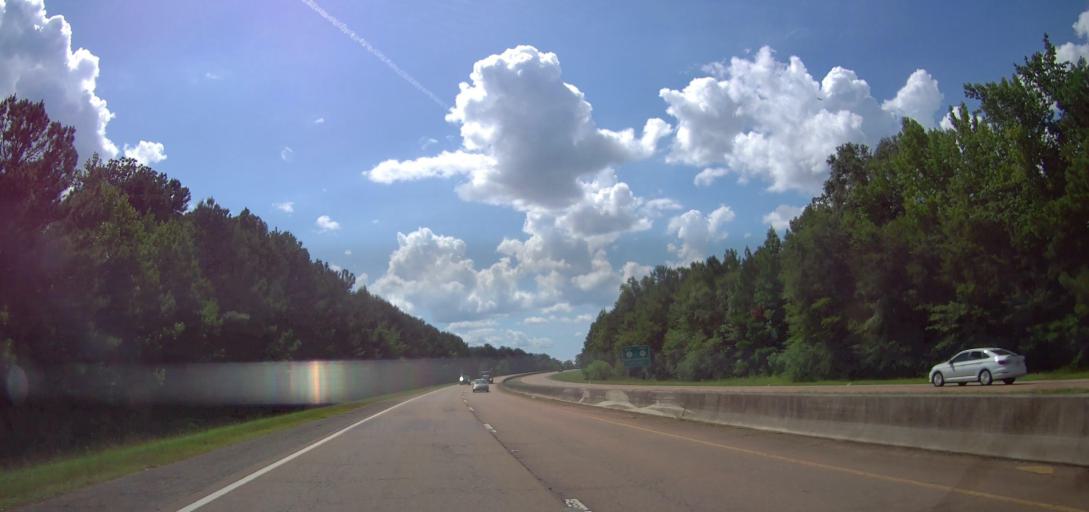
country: US
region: Mississippi
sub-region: Lowndes County
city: New Hope
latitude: 33.5082
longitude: -88.3569
